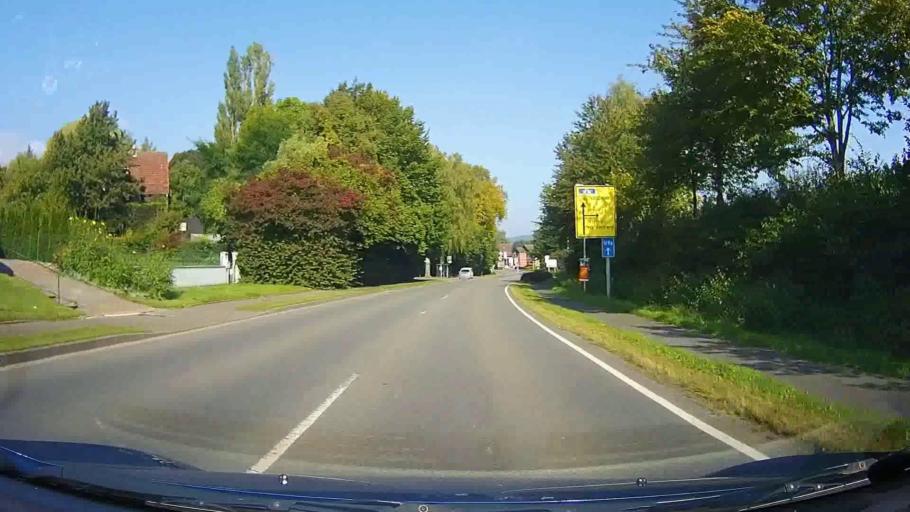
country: DE
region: Lower Saxony
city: Moringen
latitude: 51.6941
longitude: 9.8686
